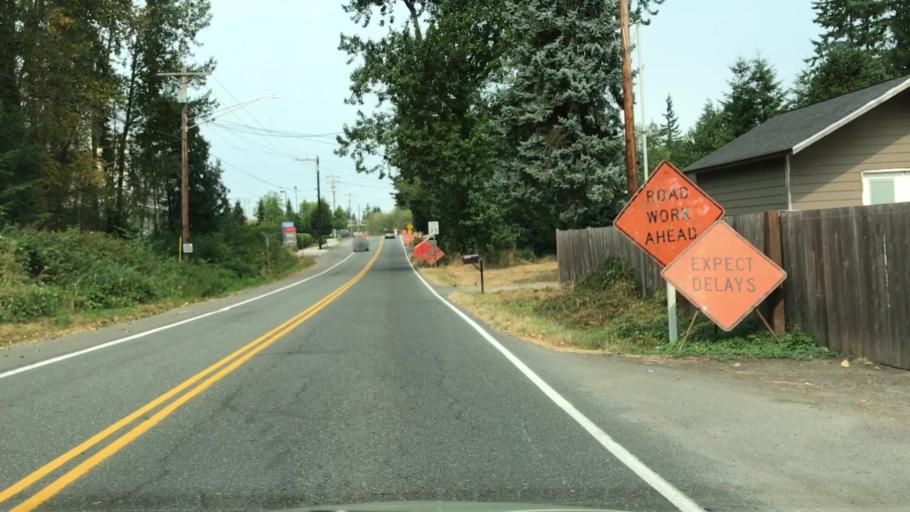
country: US
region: Washington
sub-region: Snohomish County
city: Martha Lake
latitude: 47.8772
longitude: -122.2334
